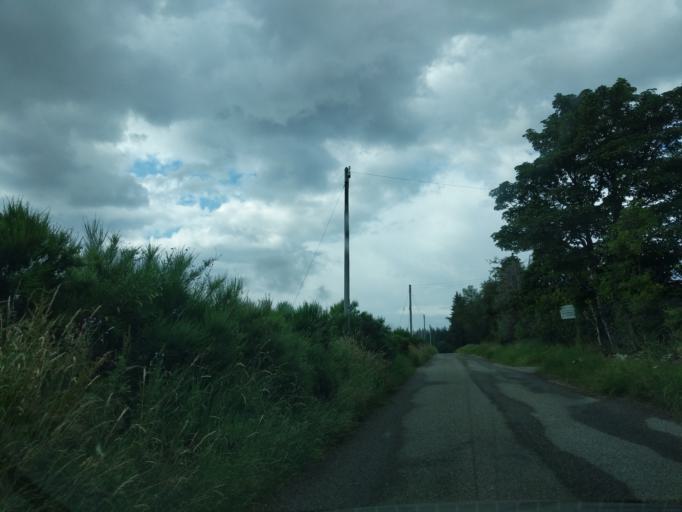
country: GB
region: Scotland
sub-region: Moray
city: Rothes
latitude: 57.4610
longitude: -3.2930
